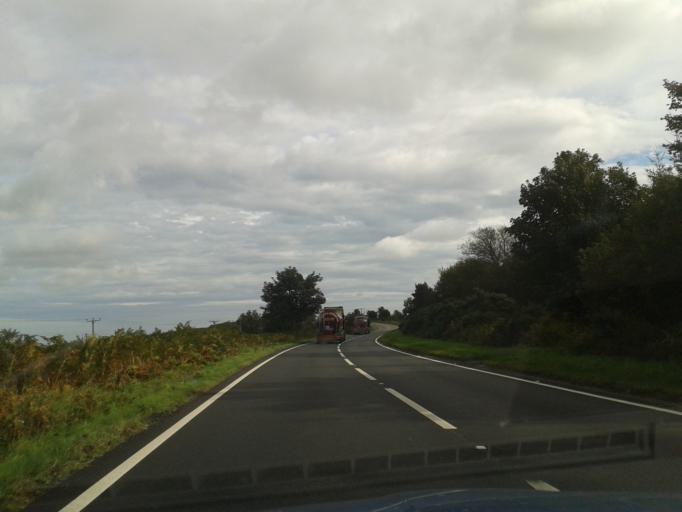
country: GB
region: Scotland
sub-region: Moray
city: Burghead
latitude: 57.6366
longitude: -3.4709
